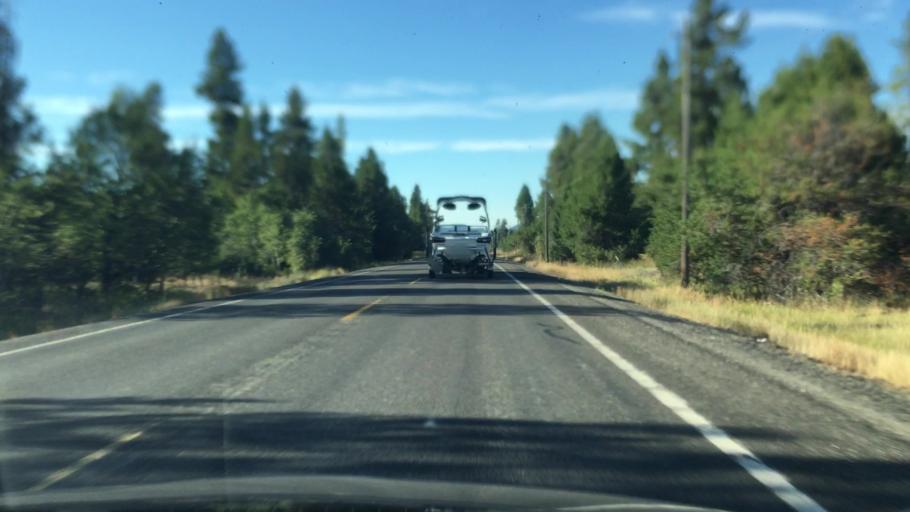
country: US
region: Idaho
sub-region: Valley County
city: Cascade
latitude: 44.4562
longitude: -115.9993
